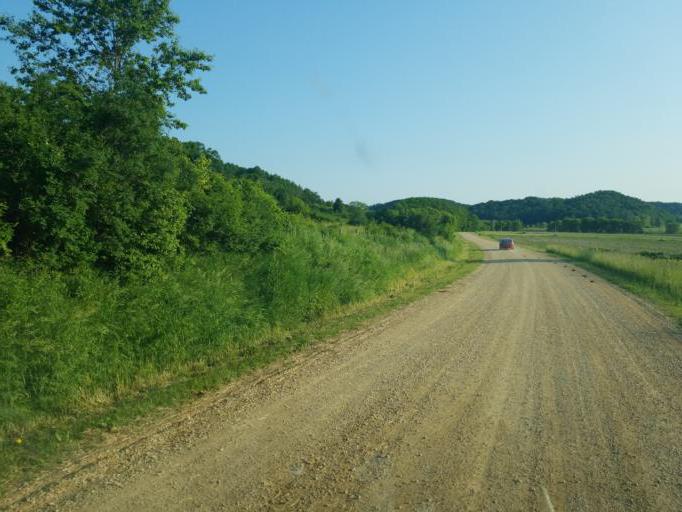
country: US
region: Wisconsin
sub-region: Vernon County
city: Hillsboro
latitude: 43.6326
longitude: -90.3551
